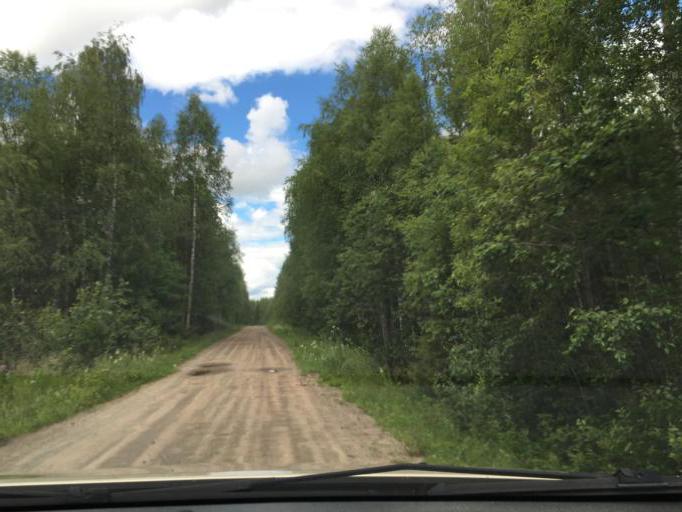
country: SE
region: Norrbotten
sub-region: Overkalix Kommun
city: OEverkalix
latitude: 66.1242
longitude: 22.7853
